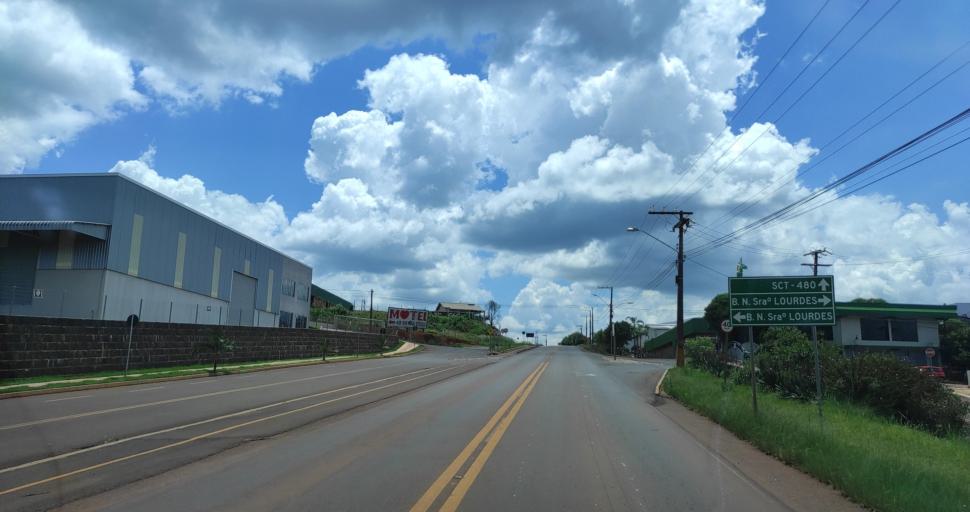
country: BR
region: Santa Catarina
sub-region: Xanxere
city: Xanxere
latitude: -26.8584
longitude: -52.4052
